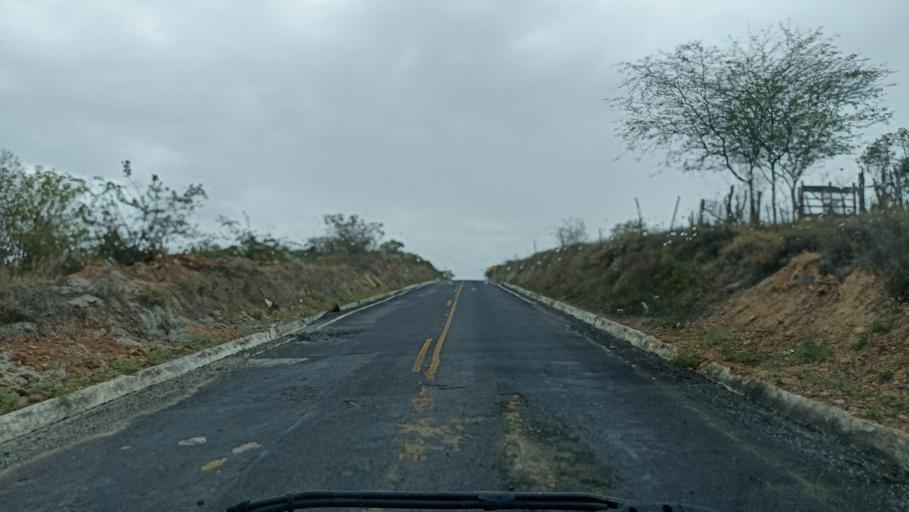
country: BR
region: Bahia
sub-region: Andarai
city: Vera Cruz
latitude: -13.0491
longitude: -40.7514
